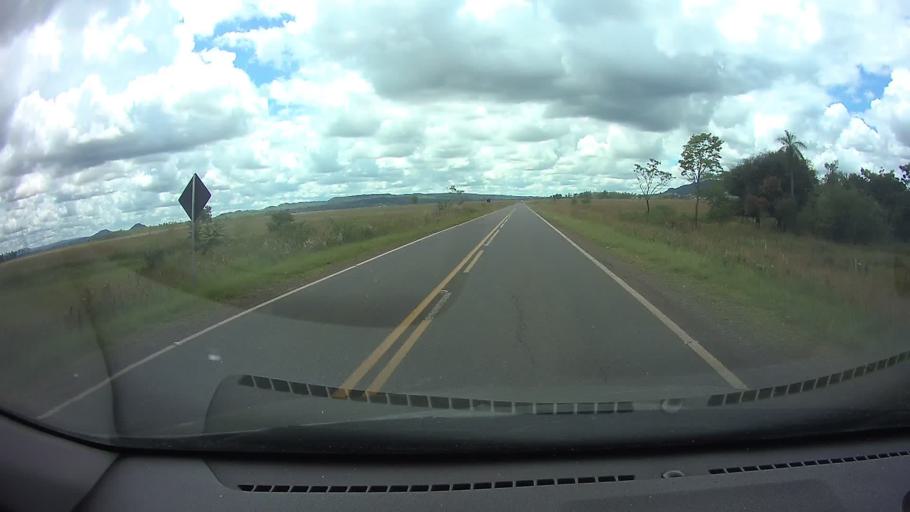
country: PY
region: Paraguari
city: Ybycui
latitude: -25.9113
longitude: -57.0205
